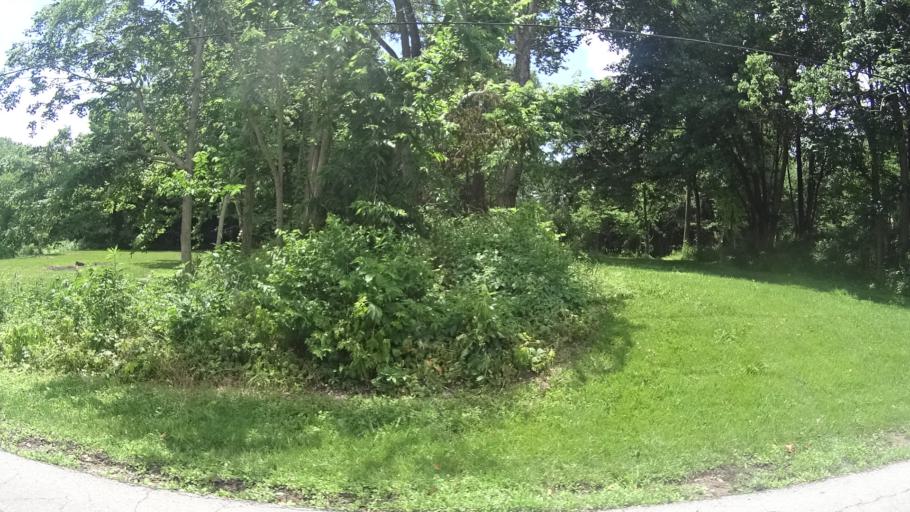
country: US
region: Ohio
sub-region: Erie County
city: Milan
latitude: 41.2999
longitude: -82.5983
